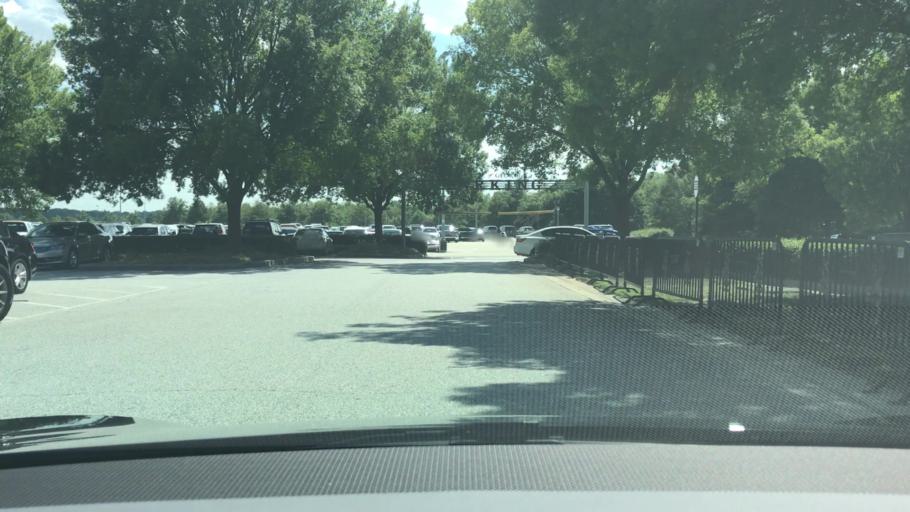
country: US
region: Georgia
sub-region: Gwinnett County
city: Buford
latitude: 34.0664
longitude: -83.9864
